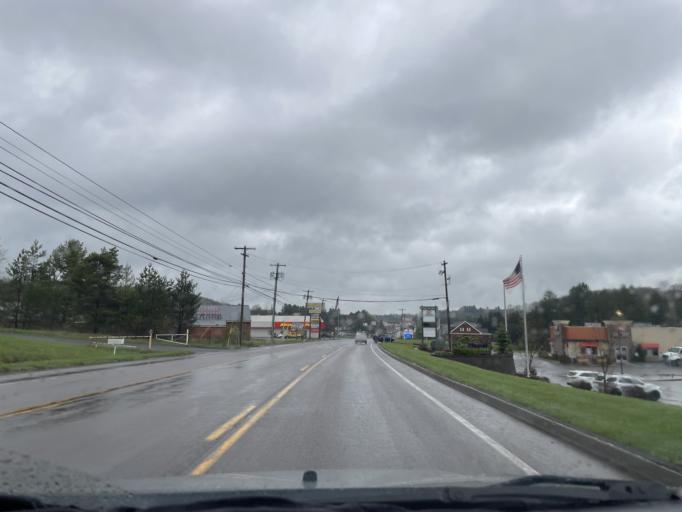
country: US
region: Maryland
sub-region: Garrett County
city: Oakland
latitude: 39.4212
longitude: -79.3983
